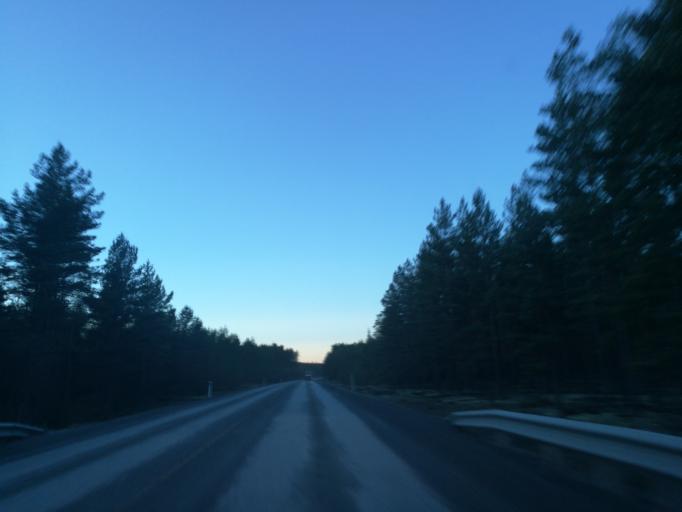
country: NO
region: Hedmark
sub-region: Eidskog
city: Skotterud
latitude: 59.9407
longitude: 12.1876
